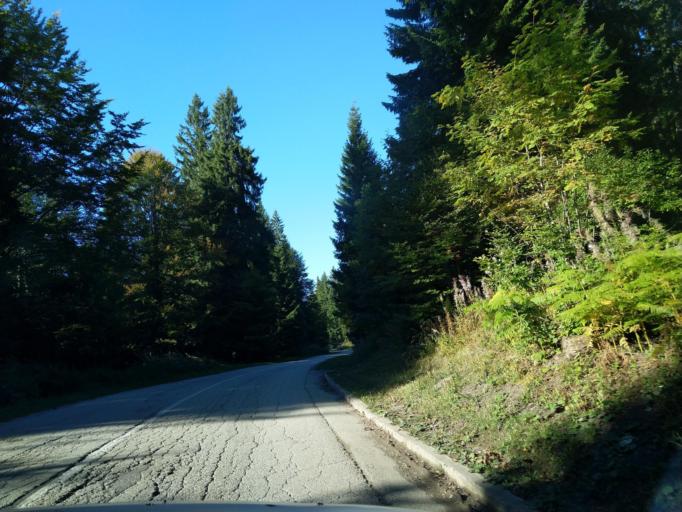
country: RS
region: Central Serbia
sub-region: Moravicki Okrug
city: Ivanjica
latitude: 43.4210
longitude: 20.2641
